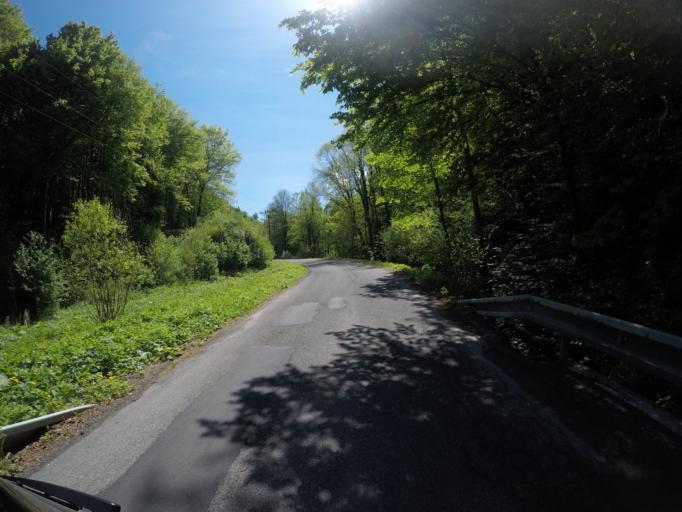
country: SK
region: Banskobystricky
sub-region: Okres Banska Bystrica
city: Banska Bystrica
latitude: 48.7305
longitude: 19.2062
